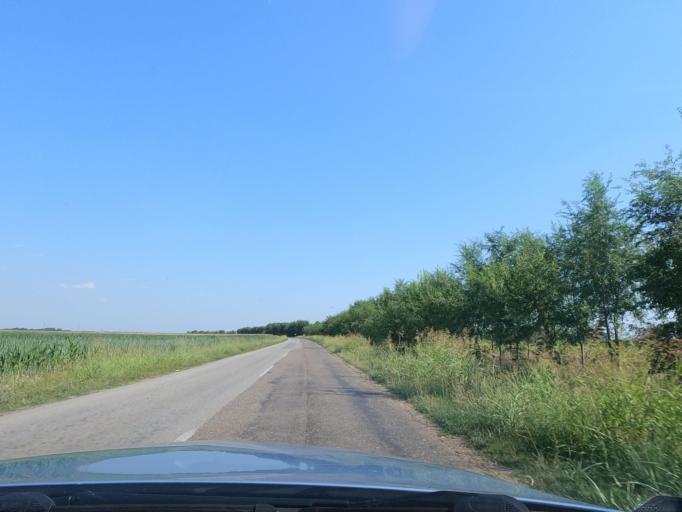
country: RS
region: Autonomna Pokrajina Vojvodina
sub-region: Juznobacki Okrug
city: Becej
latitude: 45.6551
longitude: 19.9634
